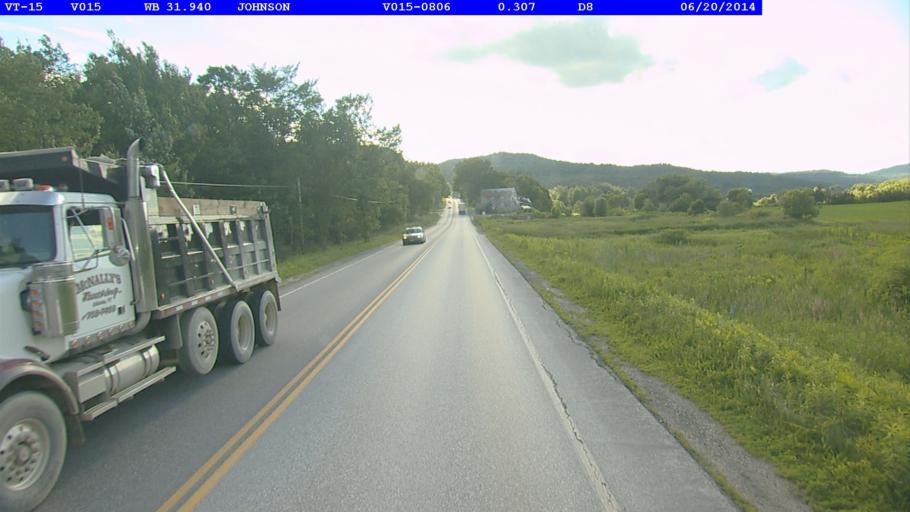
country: US
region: Vermont
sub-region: Lamoille County
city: Johnson
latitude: 44.6499
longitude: -72.7485
